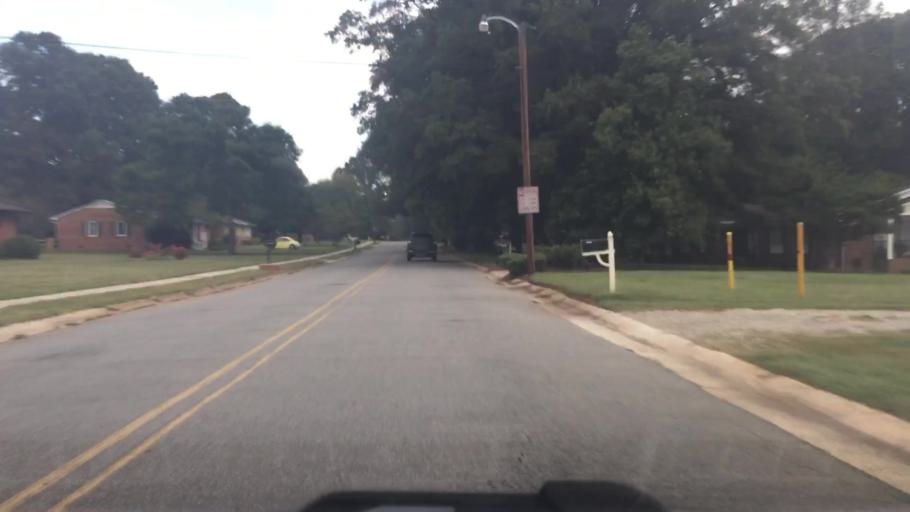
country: US
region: North Carolina
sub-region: Iredell County
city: Mooresville
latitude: 35.5650
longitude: -80.8004
